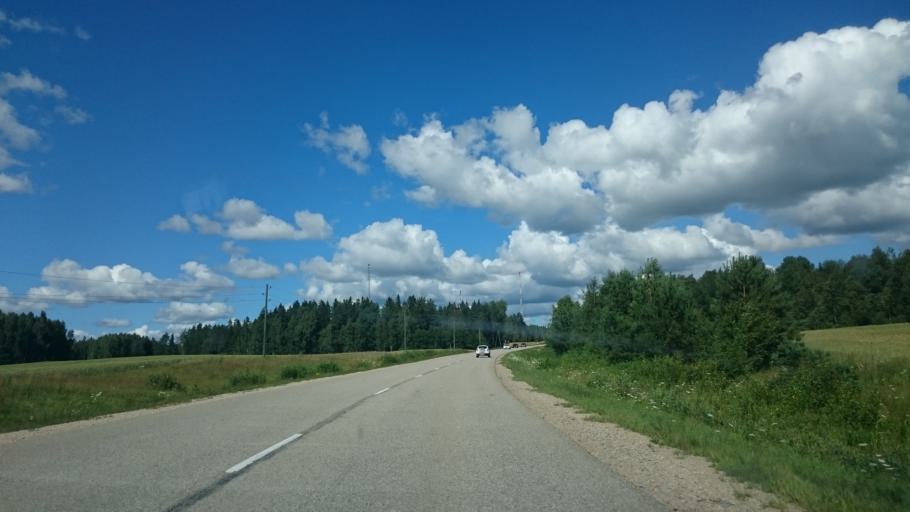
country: LV
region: Kuldigas Rajons
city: Kuldiga
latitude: 56.9204
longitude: 21.9067
